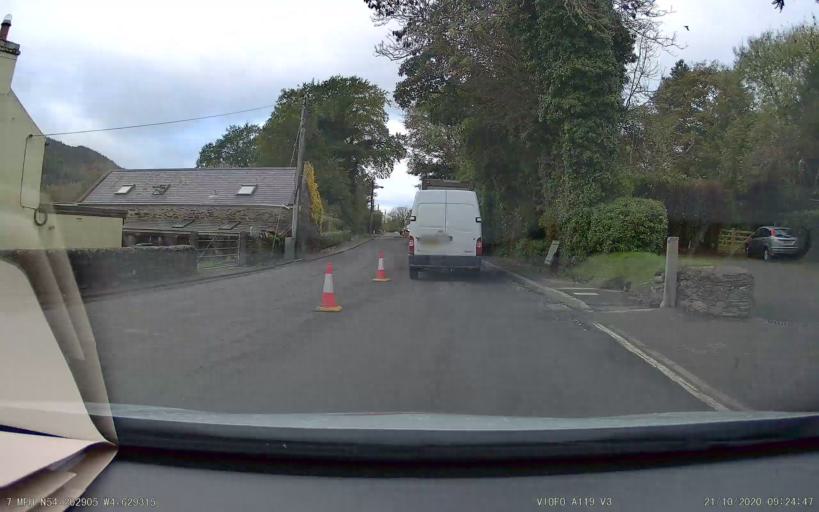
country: IM
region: Castletown
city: Castletown
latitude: 54.2029
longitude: -4.6293
